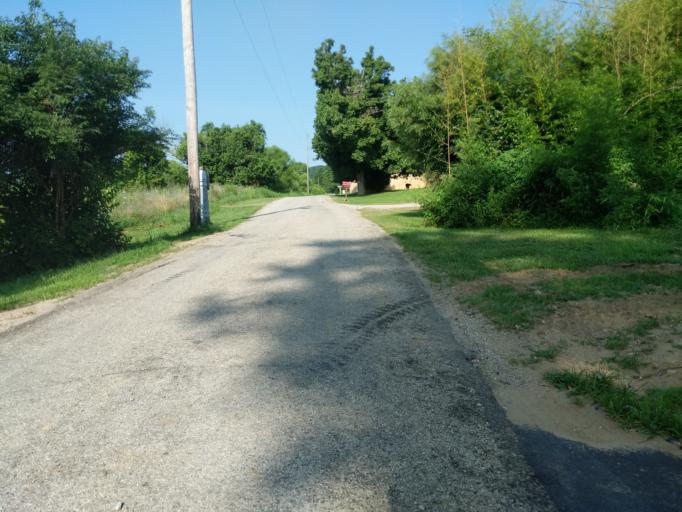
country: US
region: Ohio
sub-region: Athens County
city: Athens
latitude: 39.3457
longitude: -82.1041
